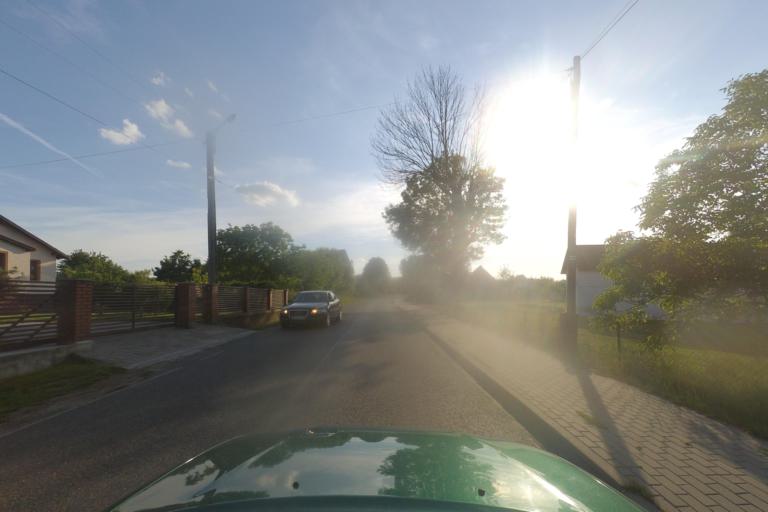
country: PL
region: Lower Silesian Voivodeship
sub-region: Powiat dzierzoniowski
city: Pilawa Gorna
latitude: 50.7215
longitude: 16.7760
